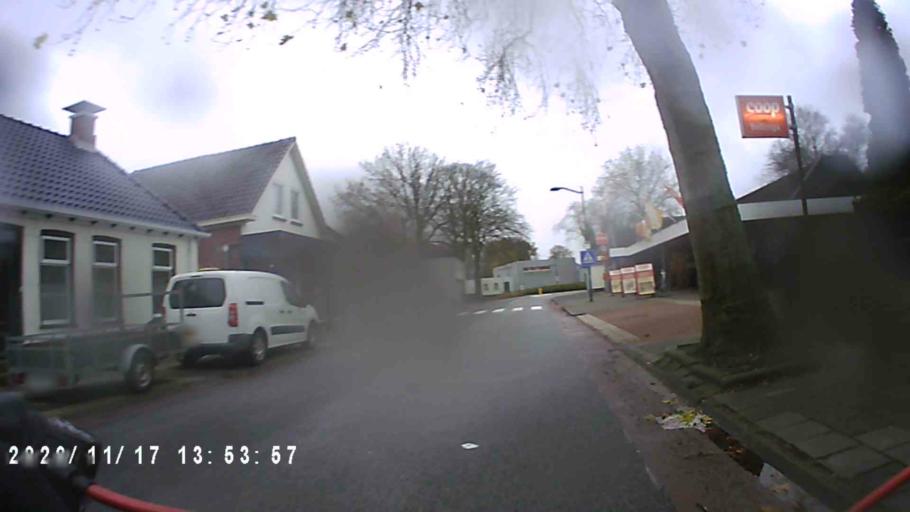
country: NL
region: Groningen
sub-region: Gemeente Zuidhorn
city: Zuidhorn
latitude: 53.2266
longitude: 6.3543
